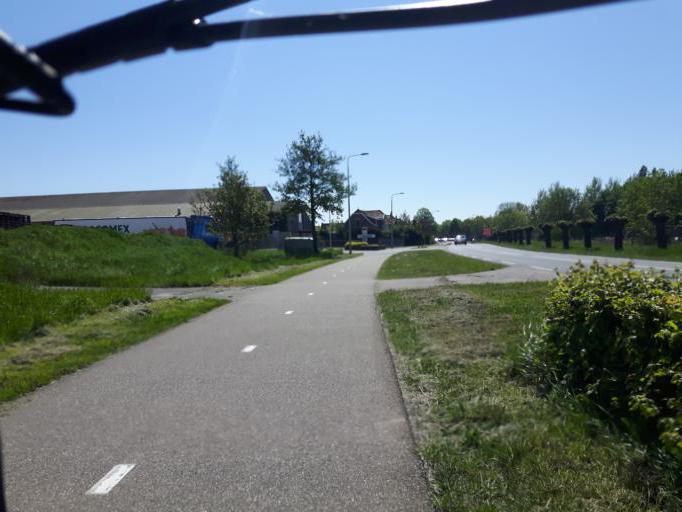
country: NL
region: Zeeland
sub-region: Gemeente Reimerswaal
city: Yerseke
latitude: 51.5550
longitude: 4.0780
